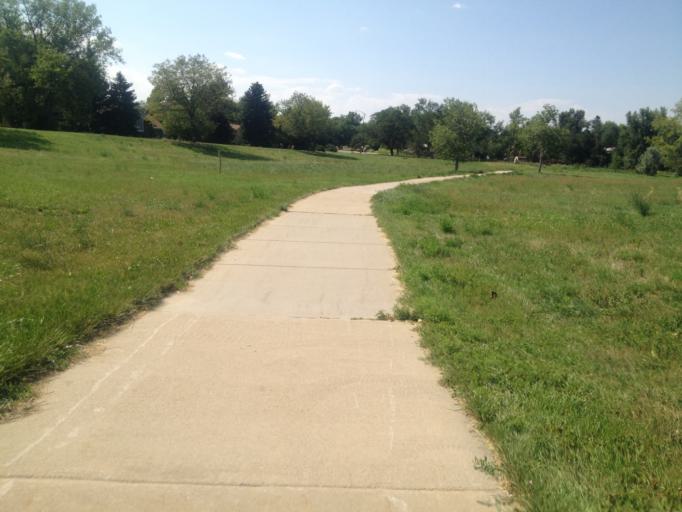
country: US
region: Colorado
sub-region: Boulder County
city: Louisville
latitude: 39.9906
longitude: -105.1348
